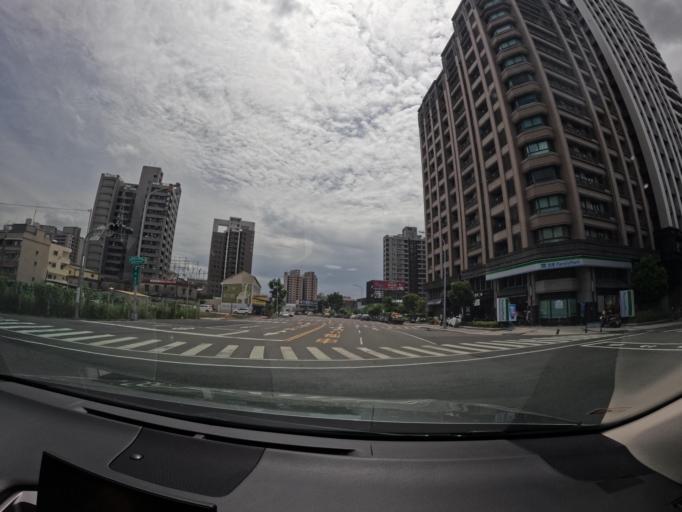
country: TW
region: Kaohsiung
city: Kaohsiung
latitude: 22.7285
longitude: 120.2845
